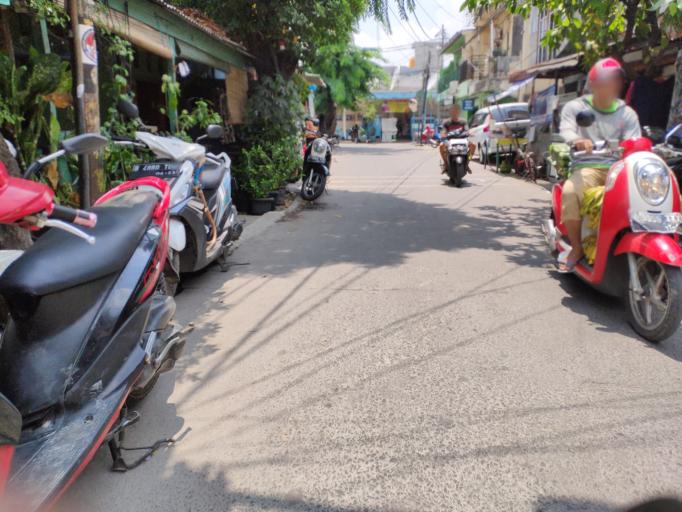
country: ID
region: Jakarta Raya
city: Jakarta
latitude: -6.2108
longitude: 106.8724
